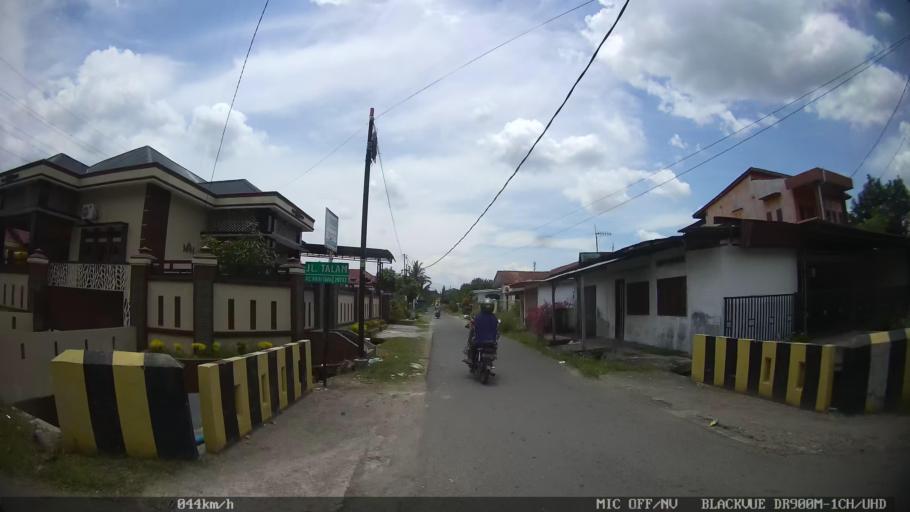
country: ID
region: North Sumatra
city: Binjai
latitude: 3.6208
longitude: 98.5038
